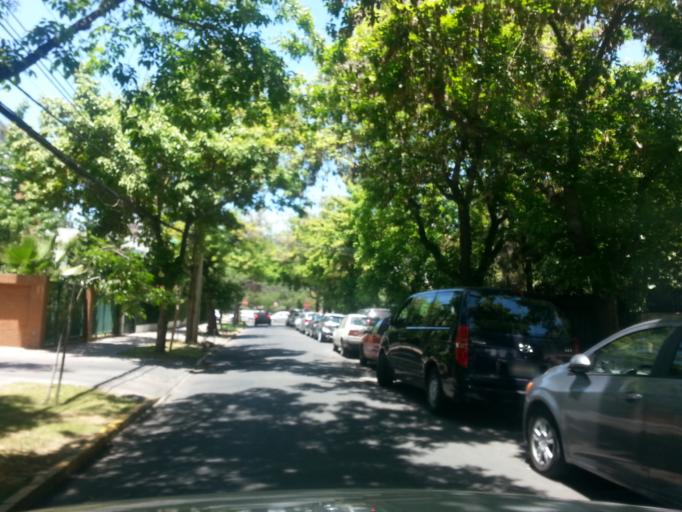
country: CL
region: Santiago Metropolitan
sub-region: Provincia de Santiago
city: Santiago
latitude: -33.4333
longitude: -70.6133
